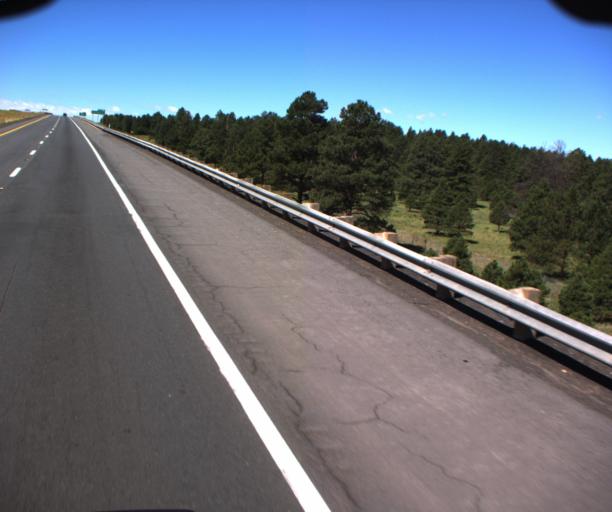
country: US
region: Arizona
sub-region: Coconino County
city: Williams
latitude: 35.2522
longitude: -112.2063
